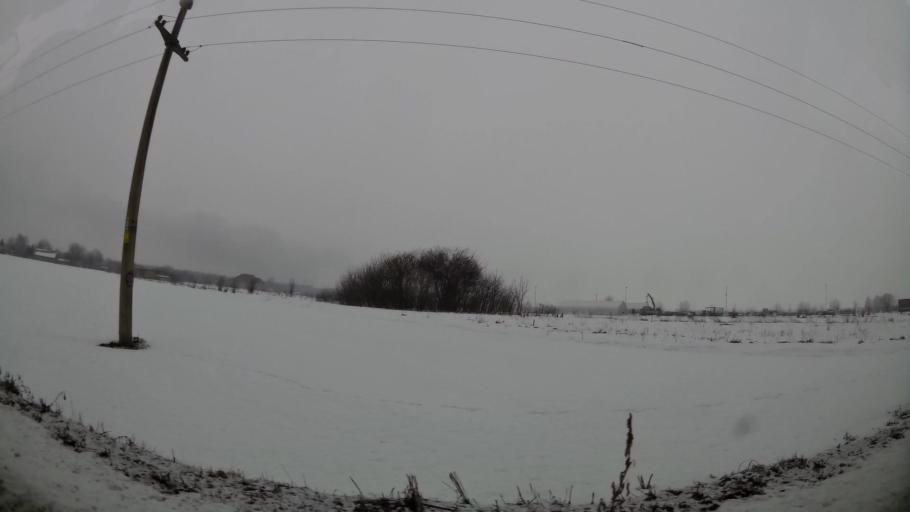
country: RS
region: Central Serbia
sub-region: Belgrade
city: Zemun
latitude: 44.8422
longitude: 20.3507
